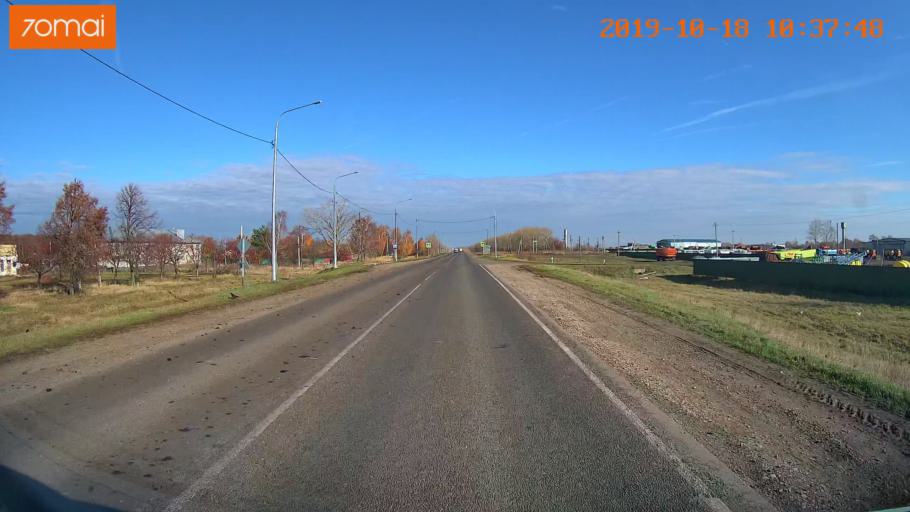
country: RU
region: Tula
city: Kurkino
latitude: 53.5650
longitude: 38.6348
